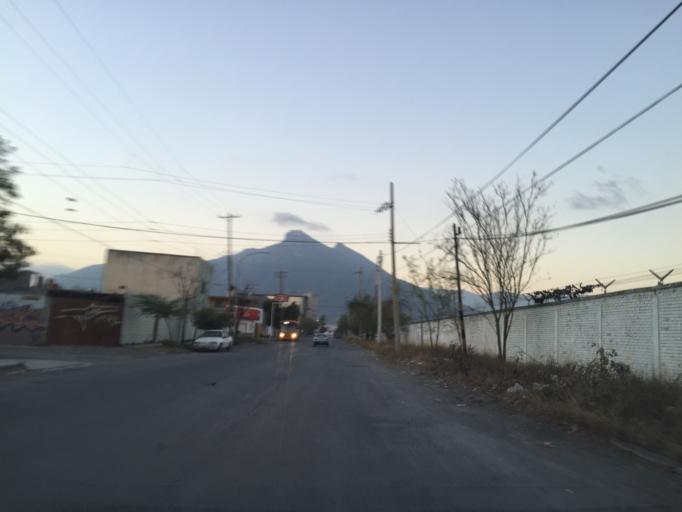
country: MX
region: Nuevo Leon
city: Guadalupe
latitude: 25.6992
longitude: -100.2230
